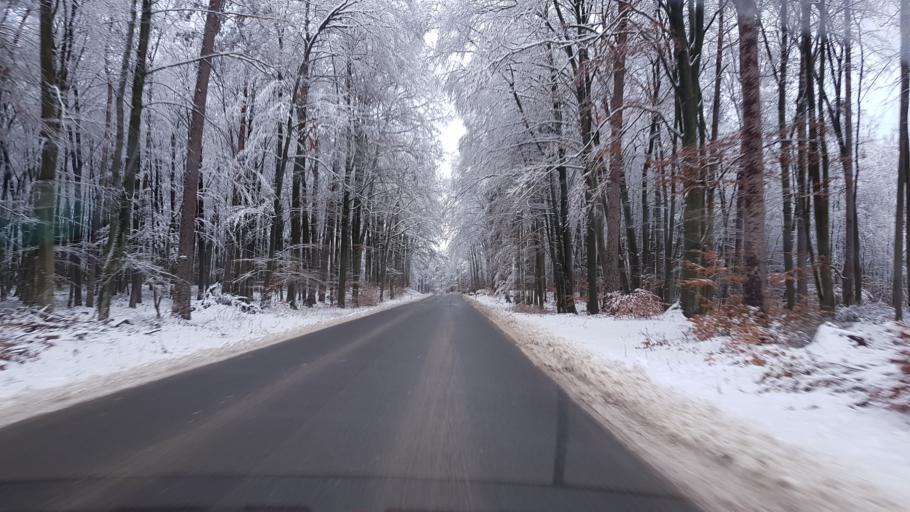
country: PL
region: West Pomeranian Voivodeship
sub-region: Powiat drawski
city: Zlocieniec
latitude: 53.5556
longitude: 16.0088
